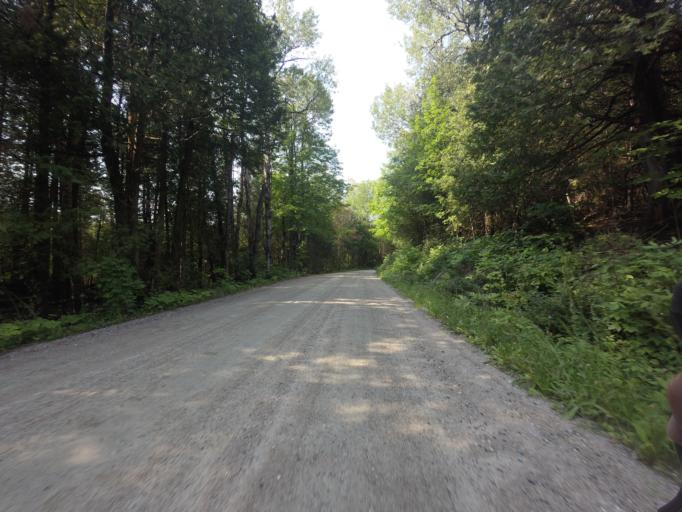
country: CA
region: Ontario
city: Skatepark
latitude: 44.7586
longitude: -76.8238
